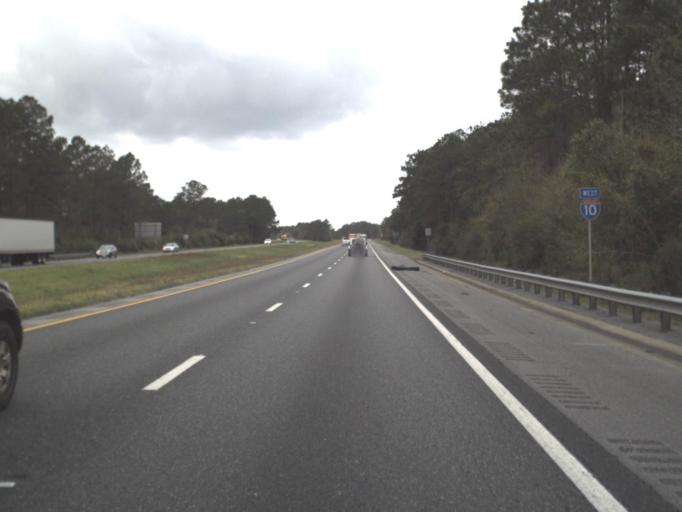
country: US
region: Florida
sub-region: Okaloosa County
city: Crestview
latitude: 30.7256
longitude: -86.5778
